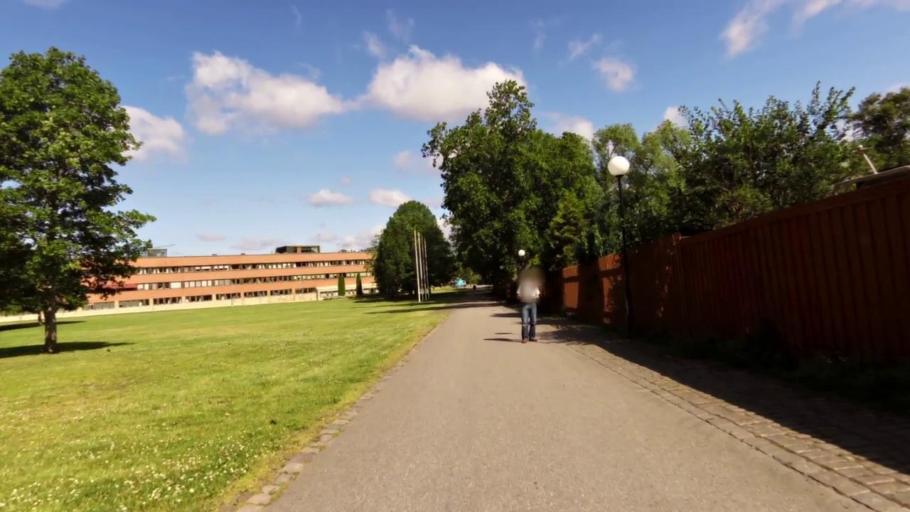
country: SE
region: OEstergoetland
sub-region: Linkopings Kommun
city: Linkoping
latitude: 58.4099
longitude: 15.6137
